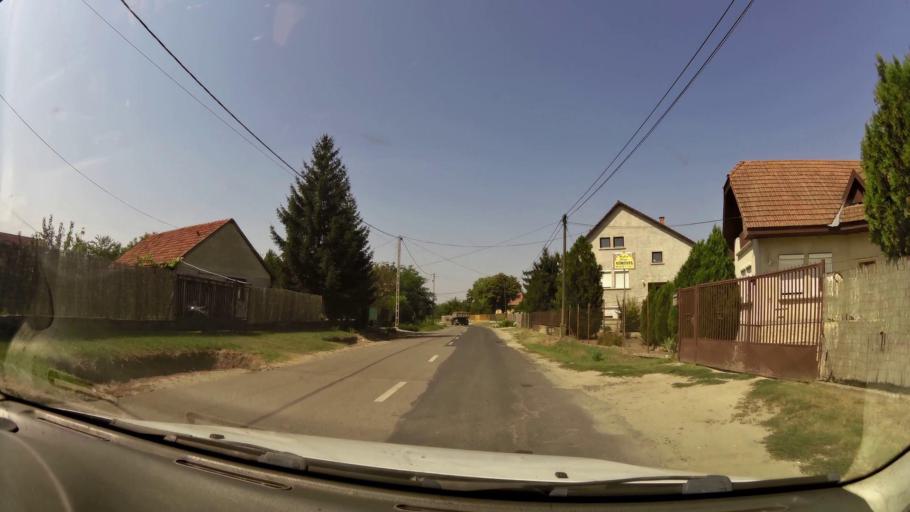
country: HU
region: Pest
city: Tapioszentmarton
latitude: 47.3443
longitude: 19.7709
